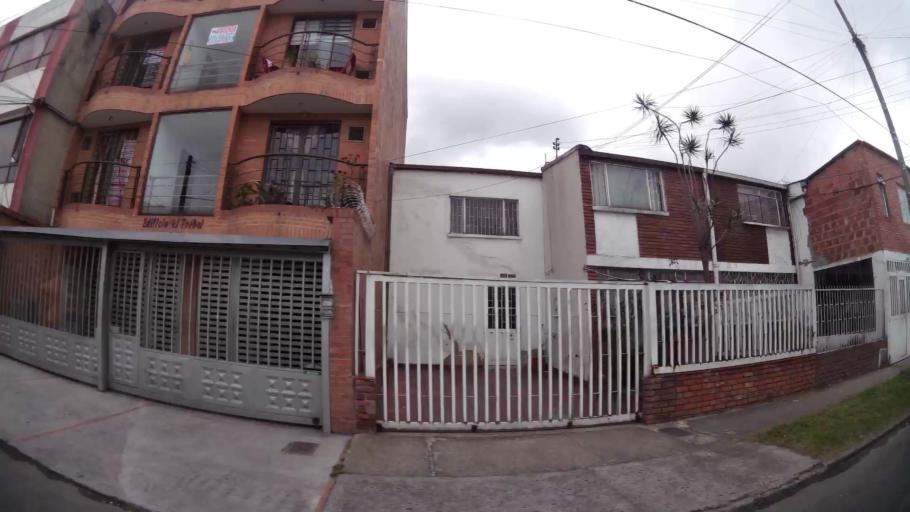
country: CO
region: Bogota D.C.
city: Bogota
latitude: 4.6709
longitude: -74.0965
